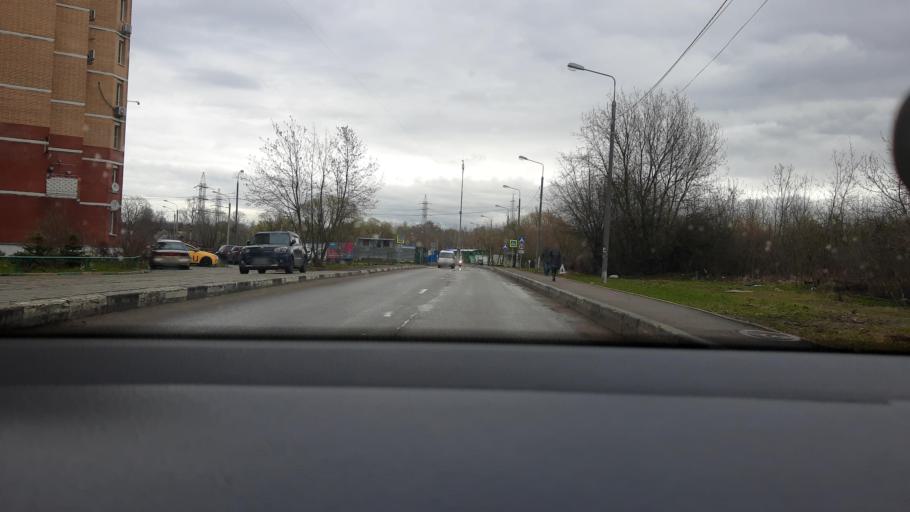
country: RU
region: Moskovskaya
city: Novopodrezkovo
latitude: 55.9202
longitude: 37.3740
